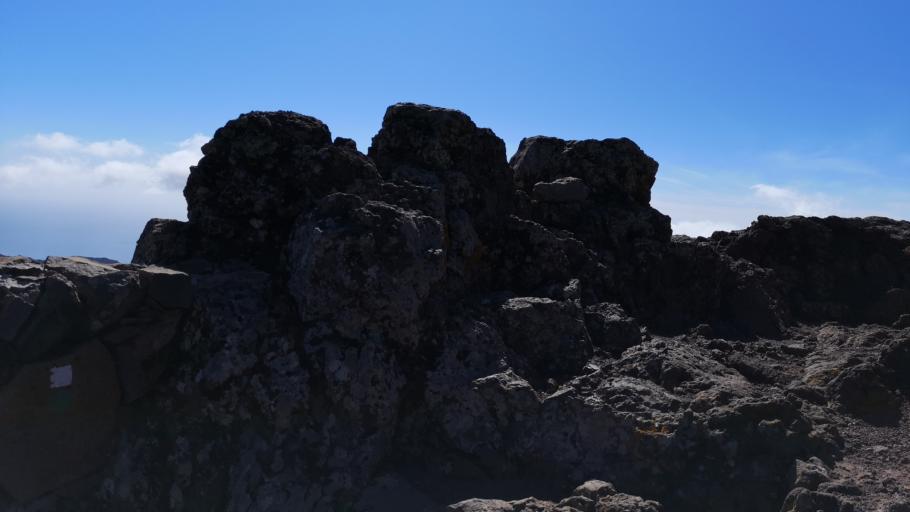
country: ES
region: Canary Islands
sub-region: Provincia de Santa Cruz de Tenerife
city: Alajero
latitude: 28.0880
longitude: -17.2351
